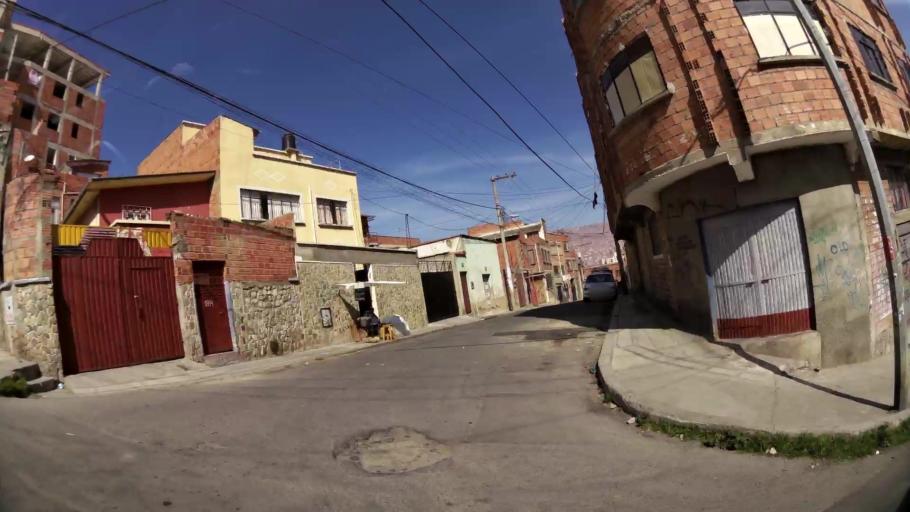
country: BO
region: La Paz
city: La Paz
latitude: -16.4985
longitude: -68.1138
